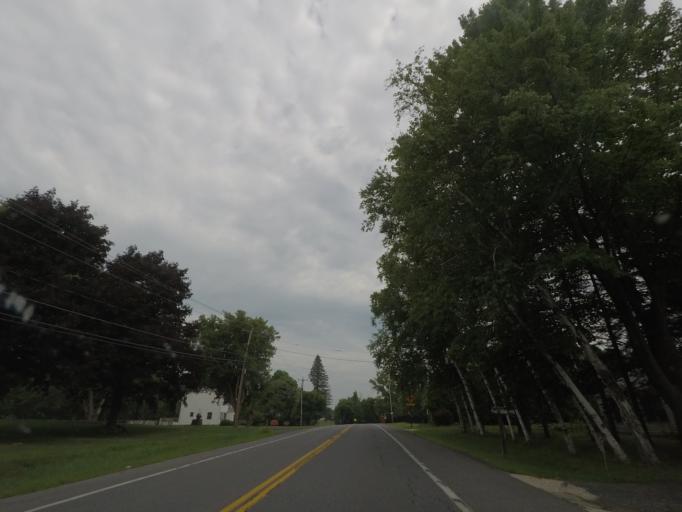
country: US
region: New York
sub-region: Saratoga County
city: Waterford
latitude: 42.8084
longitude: -73.6843
